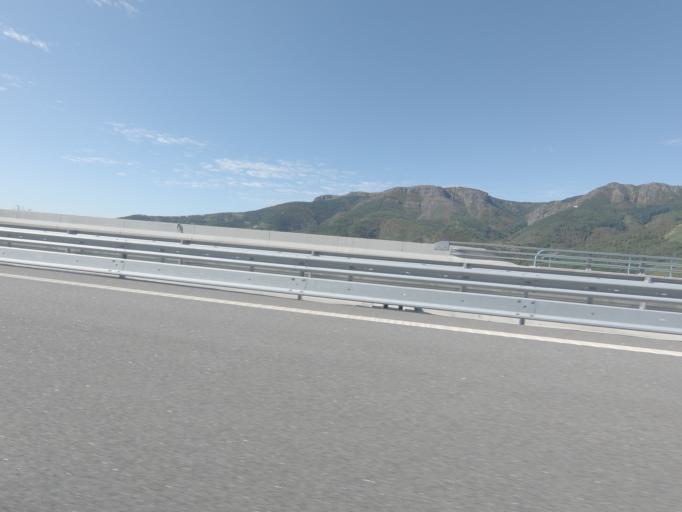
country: PT
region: Vila Real
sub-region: Santa Marta de Penaguiao
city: Santa Marta de Penaguiao
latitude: 41.2780
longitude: -7.8616
